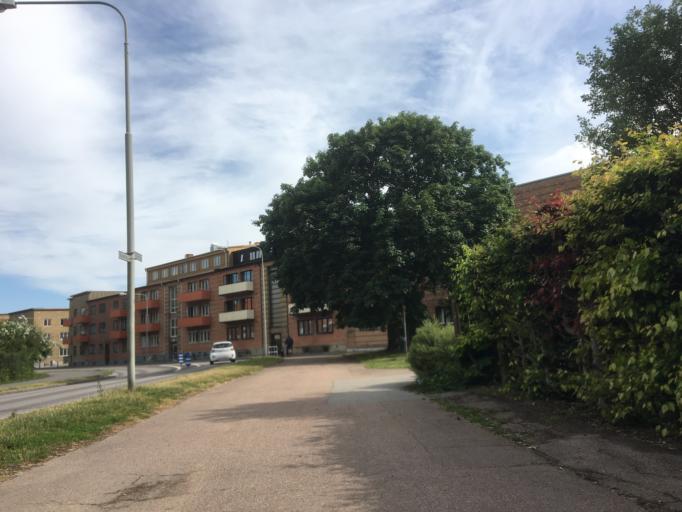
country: SE
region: Skane
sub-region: Landskrona
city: Landskrona
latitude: 55.8774
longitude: 12.8389
